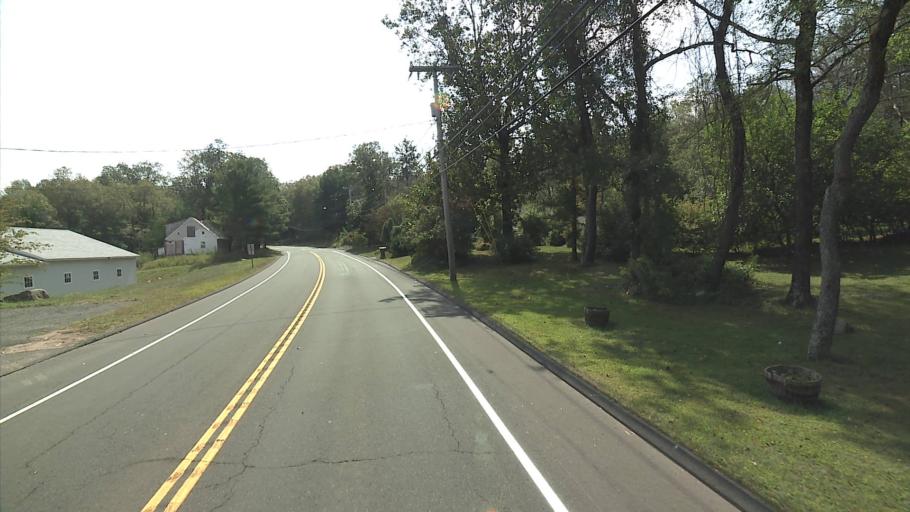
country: US
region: Connecticut
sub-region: Middlesex County
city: Durham
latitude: 41.4108
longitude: -72.6567
